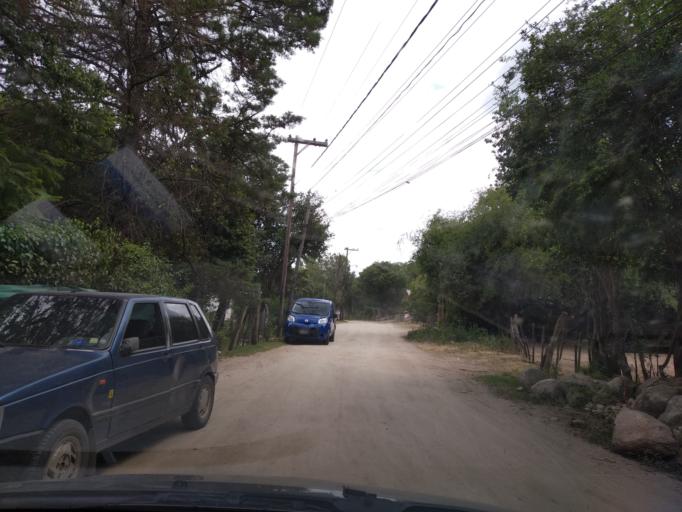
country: AR
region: Cordoba
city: Villa Las Rosas
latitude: -31.9414
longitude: -65.0308
